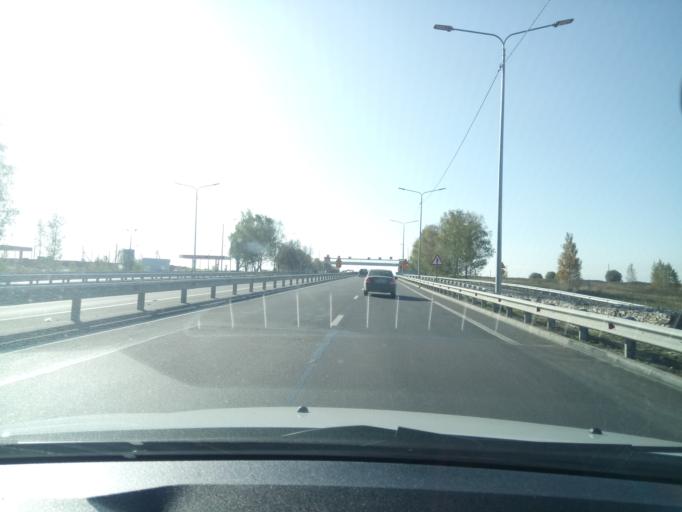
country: RU
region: Nizjnij Novgorod
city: Burevestnik
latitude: 56.0024
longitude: 43.9673
